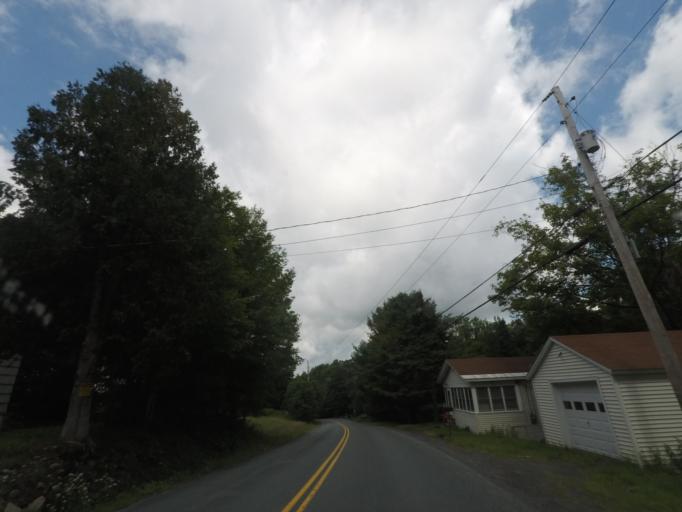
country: US
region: New York
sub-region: Rensselaer County
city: Averill Park
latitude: 42.6423
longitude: -73.4734
